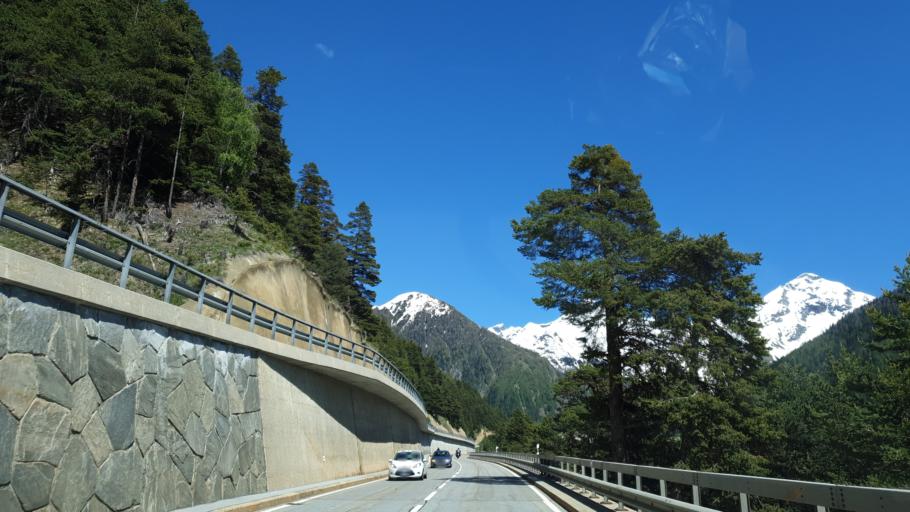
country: CH
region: Valais
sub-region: Brig District
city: Naters
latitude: 46.2969
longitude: 8.0321
